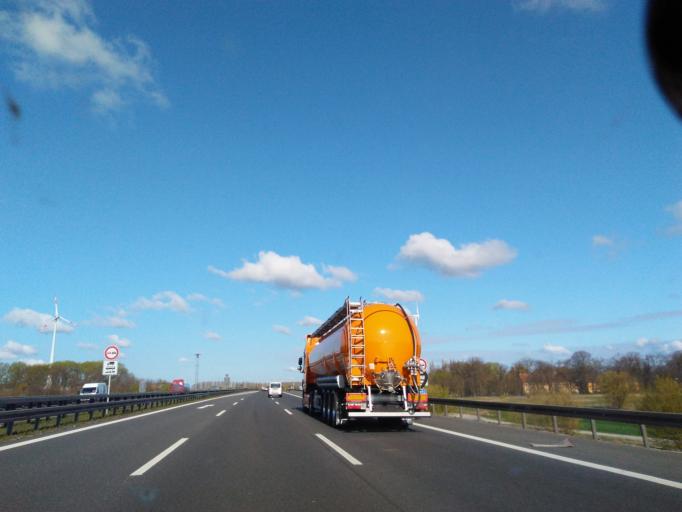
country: DE
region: Berlin
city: Buchholz
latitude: 52.6343
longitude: 13.4452
